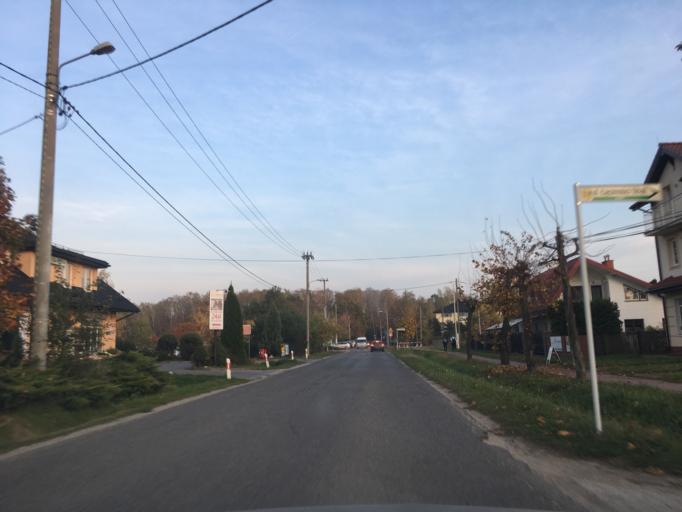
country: PL
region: Masovian Voivodeship
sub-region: Powiat piaseczynski
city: Lesznowola
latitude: 52.0792
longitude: 20.8898
